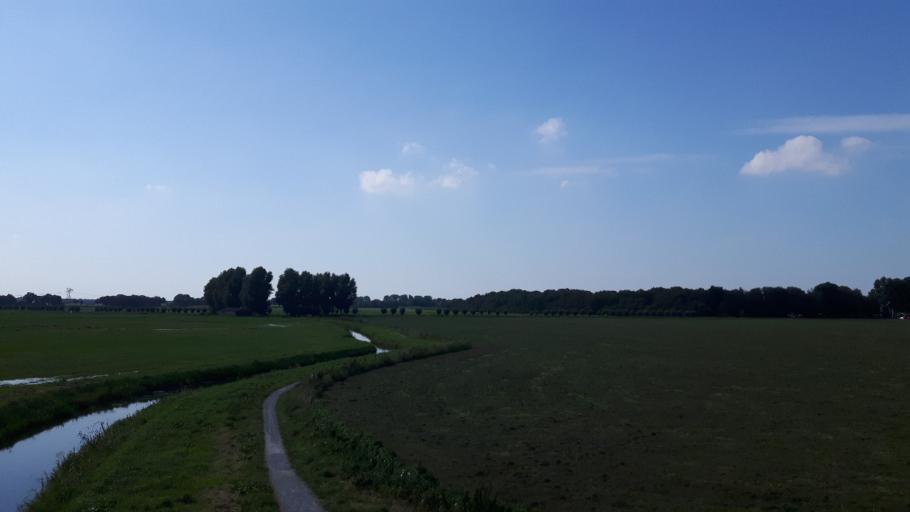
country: NL
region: Drenthe
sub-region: Gemeente Tynaarlo
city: Zuidlaren
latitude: 53.1063
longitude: 6.7044
